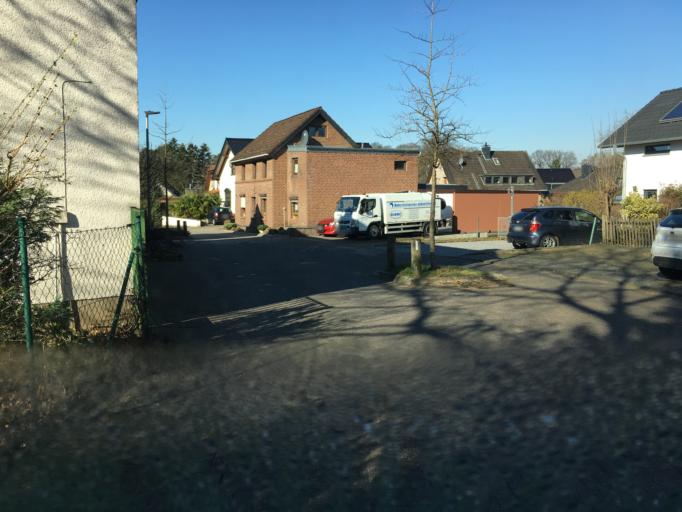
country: DE
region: North Rhine-Westphalia
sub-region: Regierungsbezirk Koln
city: Odenthal
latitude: 51.0153
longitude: 7.0756
